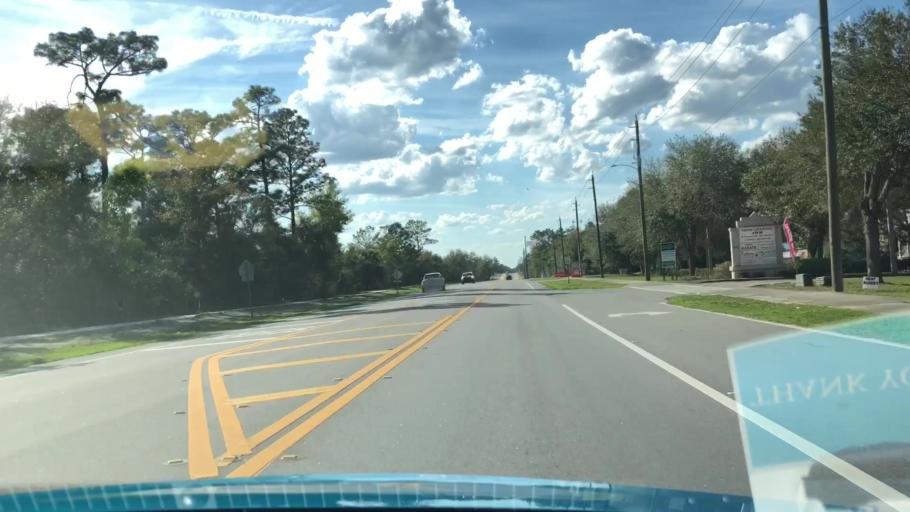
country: US
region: Florida
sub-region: Seminole County
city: Midway
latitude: 28.8567
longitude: -81.1872
